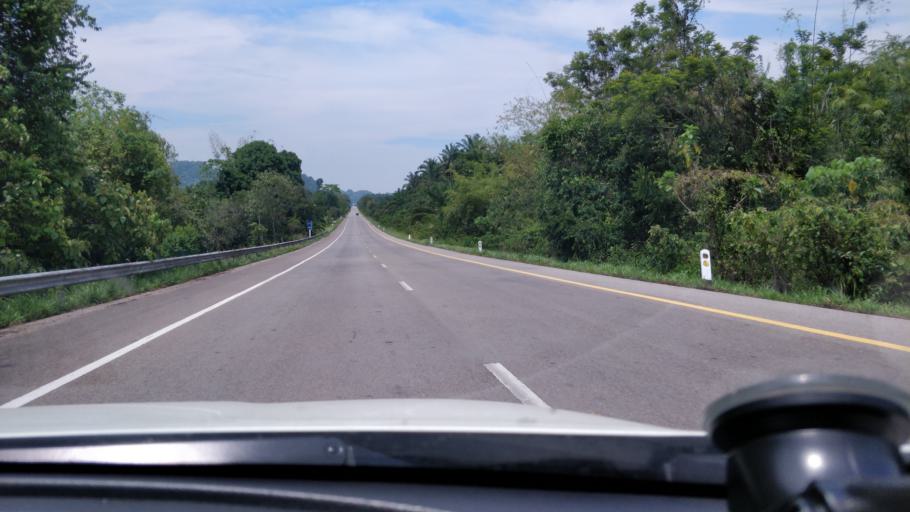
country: TH
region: Krabi
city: Plai Phraya
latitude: 8.5643
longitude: 98.9224
